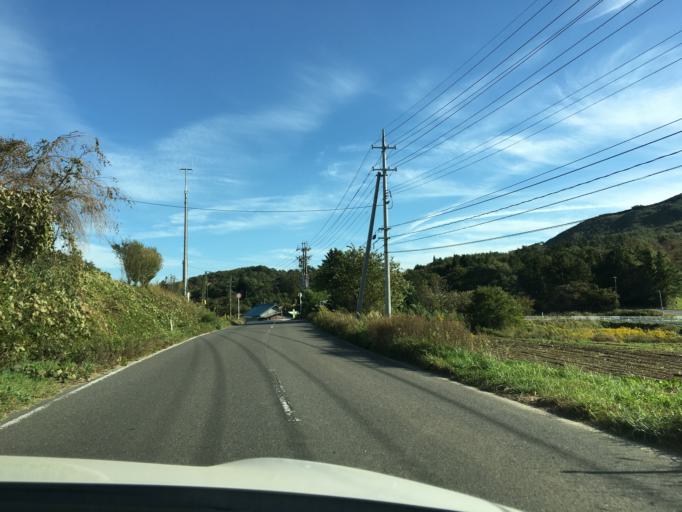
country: JP
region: Fukushima
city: Funehikimachi-funehiki
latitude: 37.3365
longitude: 140.5743
